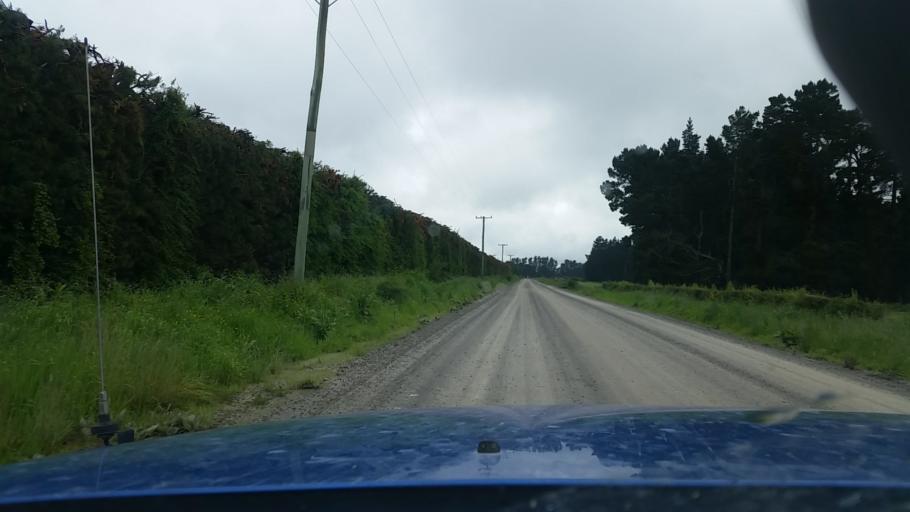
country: NZ
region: Canterbury
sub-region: Ashburton District
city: Methven
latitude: -43.6125
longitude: 171.4852
